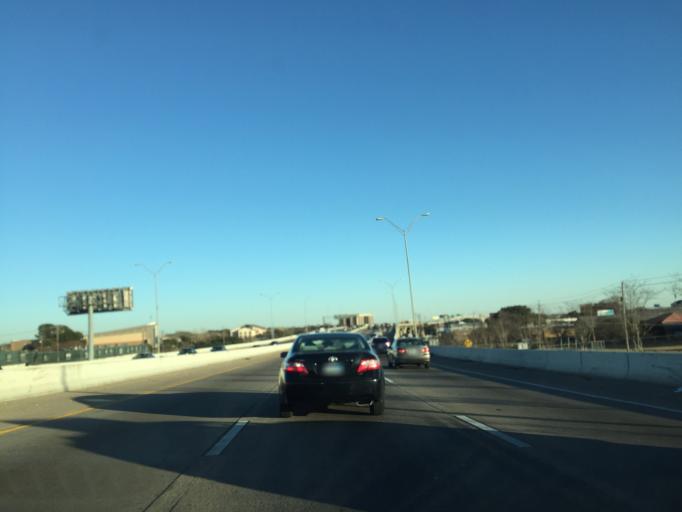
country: US
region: Texas
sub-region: Travis County
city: Austin
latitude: 30.3459
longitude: -97.7091
